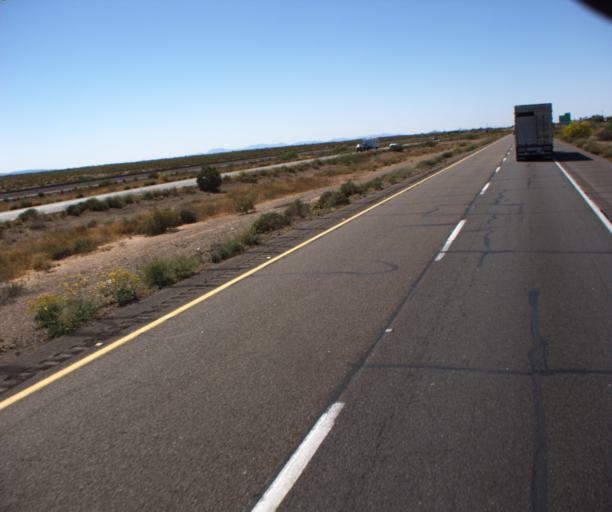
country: US
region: Arizona
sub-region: Maricopa County
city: Gila Bend
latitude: 32.8600
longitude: -113.1976
